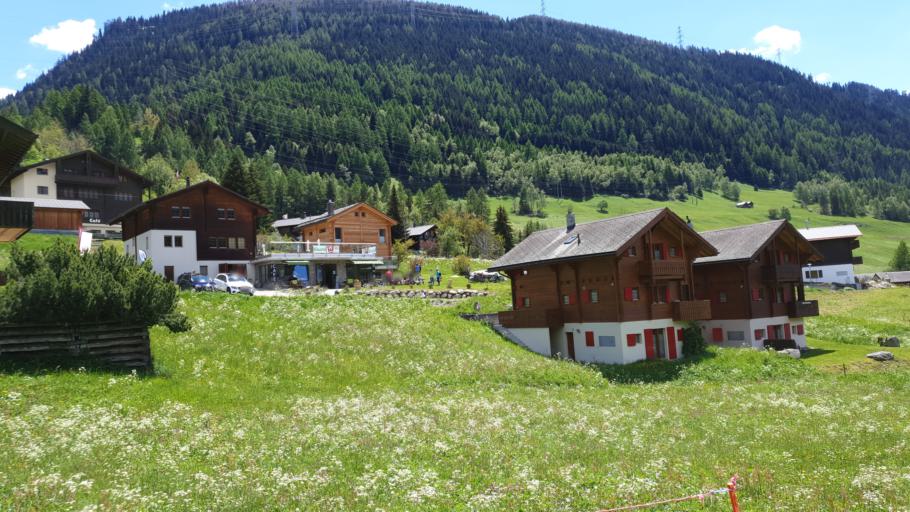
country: CH
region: Valais
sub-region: Goms District
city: Fiesch
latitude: 46.4091
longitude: 8.1544
